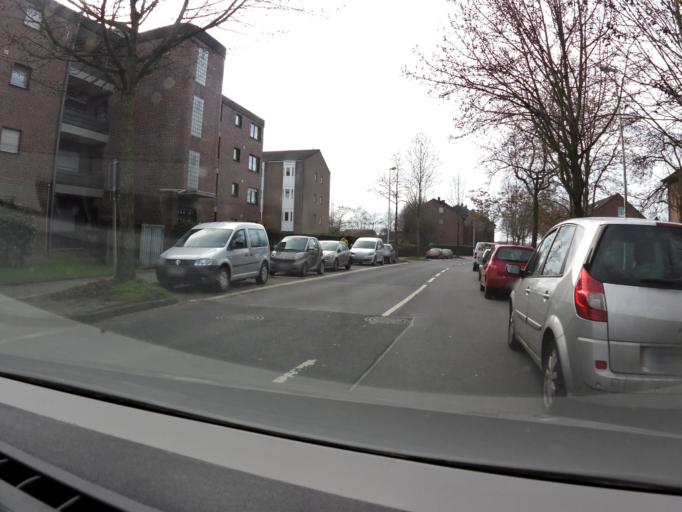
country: DE
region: North Rhine-Westphalia
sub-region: Regierungsbezirk Dusseldorf
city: Nettetal
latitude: 51.2998
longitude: 6.2739
